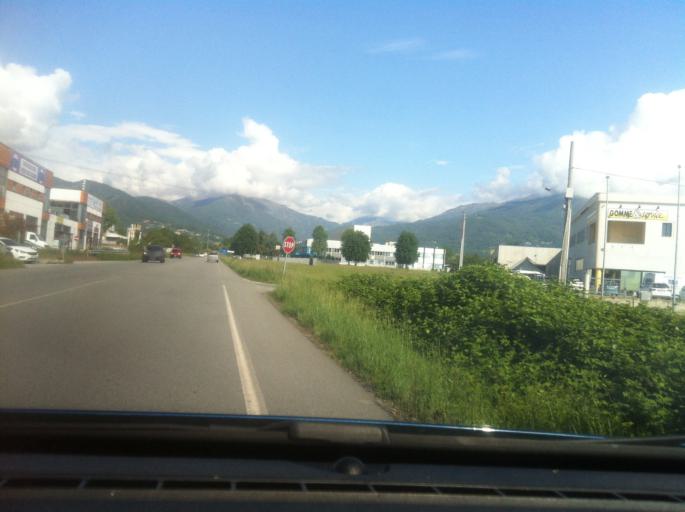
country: IT
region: Piedmont
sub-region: Provincia di Torino
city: Salassa
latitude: 45.3687
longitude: 7.6792
